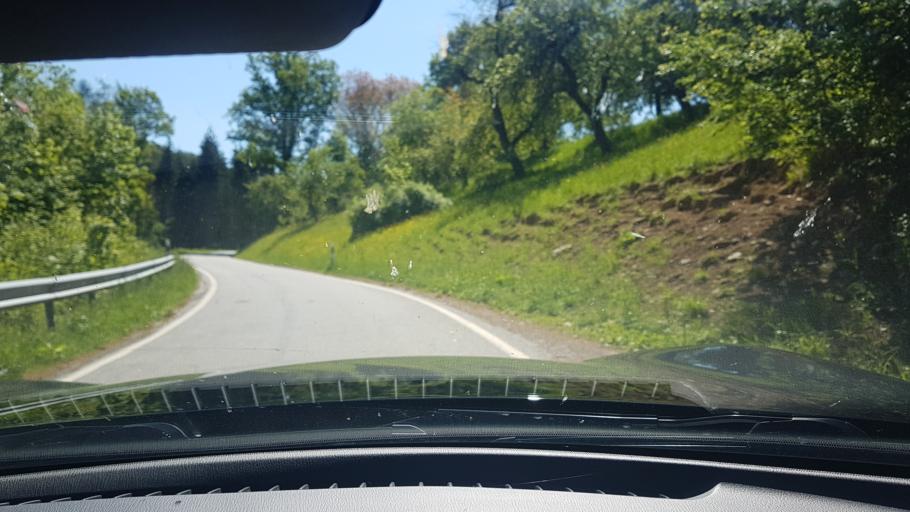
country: DE
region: Baden-Wuerttemberg
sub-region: Karlsruhe Region
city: Adelsheim
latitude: 49.4046
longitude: 9.4054
